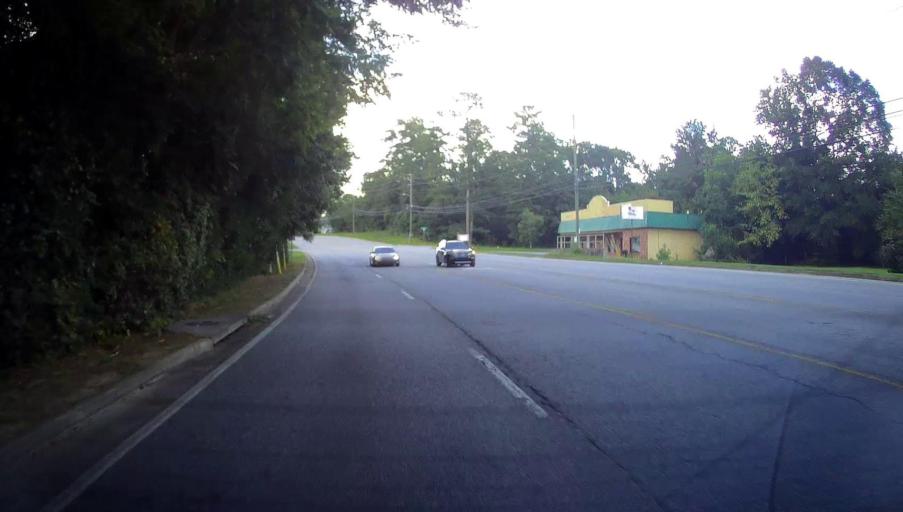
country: US
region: Georgia
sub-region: Muscogee County
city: Columbus
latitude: 32.5306
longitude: -84.9093
